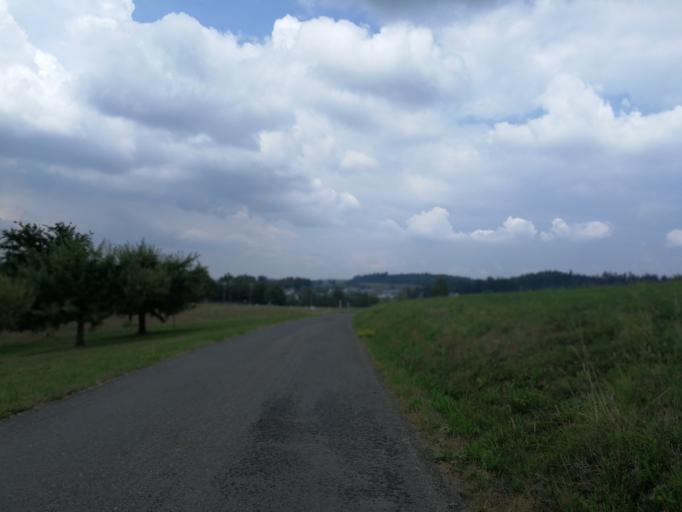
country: CH
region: Zurich
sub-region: Bezirk Hinwil
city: Gossau
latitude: 47.2967
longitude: 8.7734
